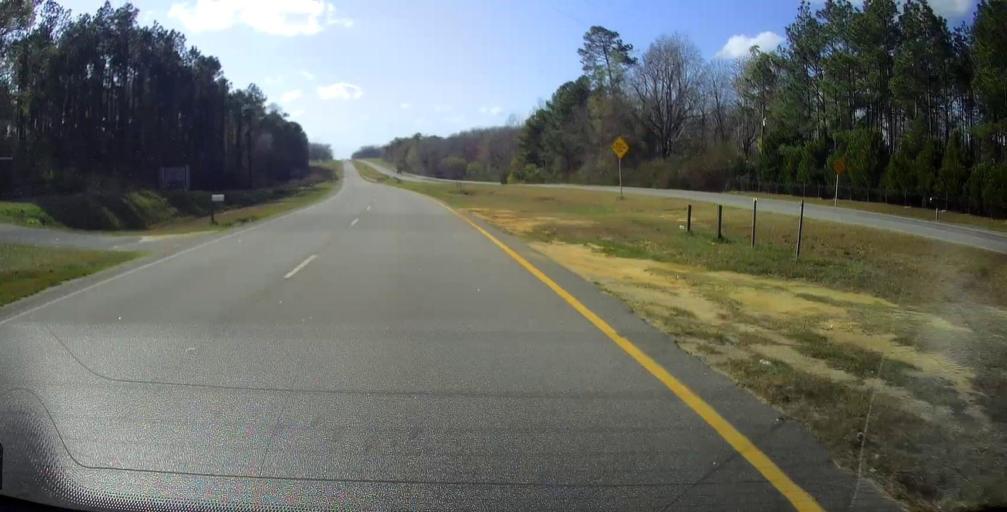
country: US
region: Georgia
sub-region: Dodge County
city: Eastman
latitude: 32.1972
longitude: -83.2133
